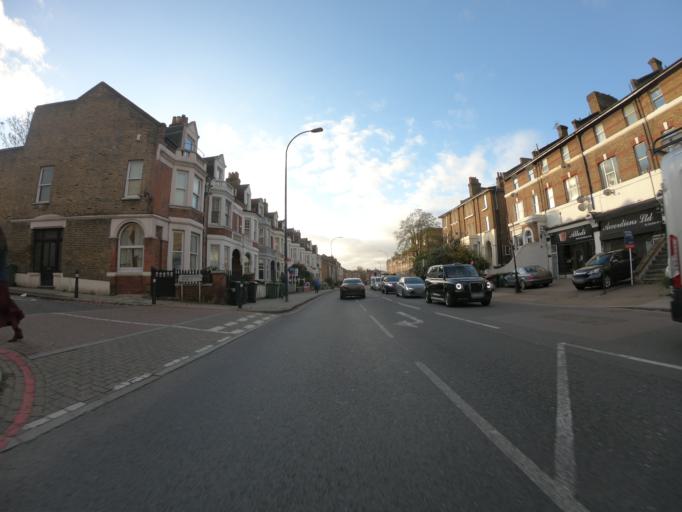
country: GB
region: England
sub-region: Greater London
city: Blackheath
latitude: 51.4585
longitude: 0.0011
